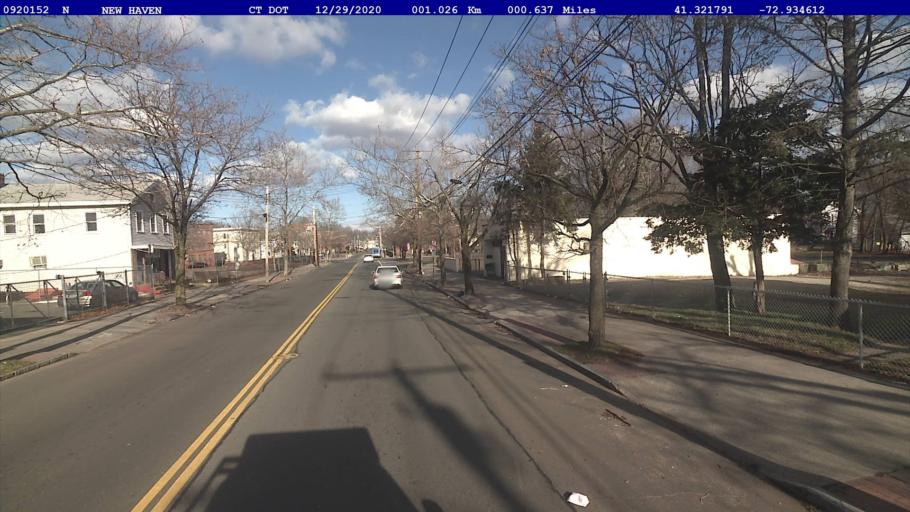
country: US
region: Connecticut
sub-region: New Haven County
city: New Haven
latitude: 41.3218
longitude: -72.9346
